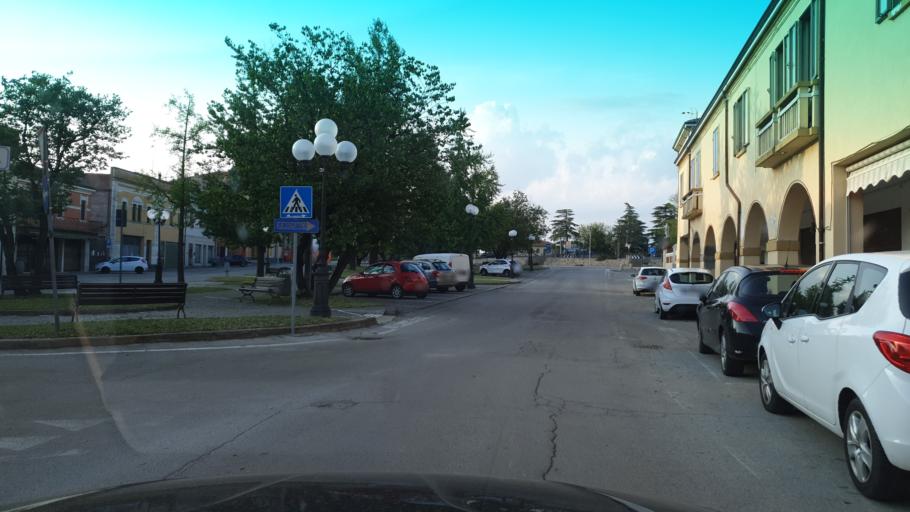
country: IT
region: Veneto
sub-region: Provincia di Rovigo
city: Castelguglielmo
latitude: 45.0245
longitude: 11.5375
